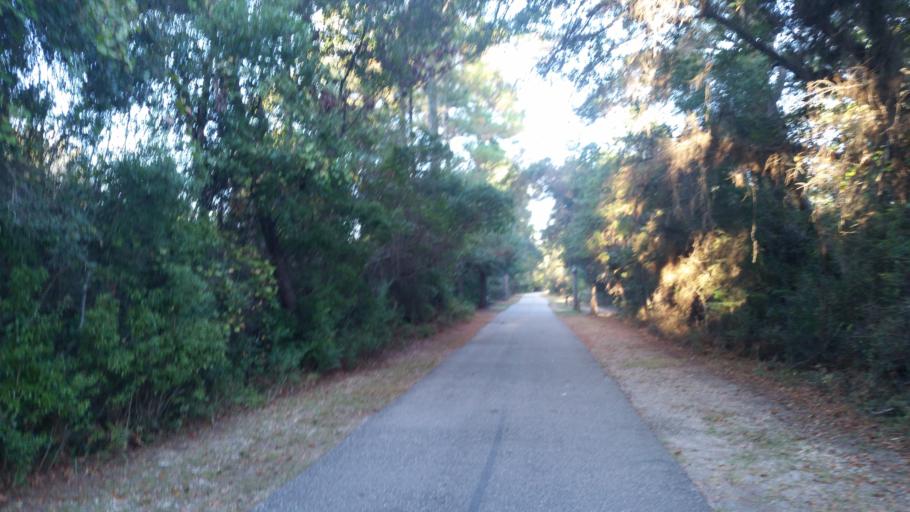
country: US
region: Alabama
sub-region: Baldwin County
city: Orange Beach
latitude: 30.2793
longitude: -87.5860
